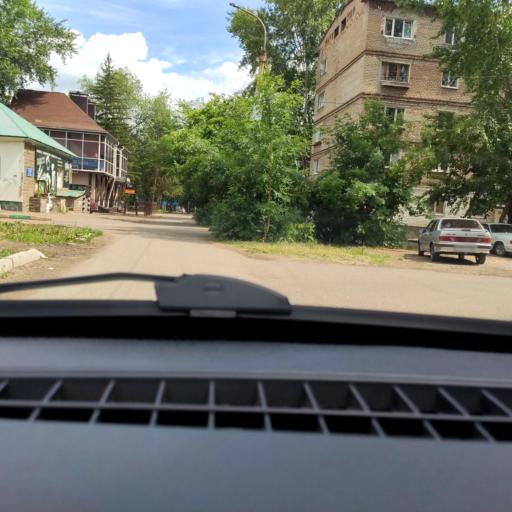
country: RU
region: Bashkortostan
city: Sterlitamak
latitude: 53.6355
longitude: 55.9323
